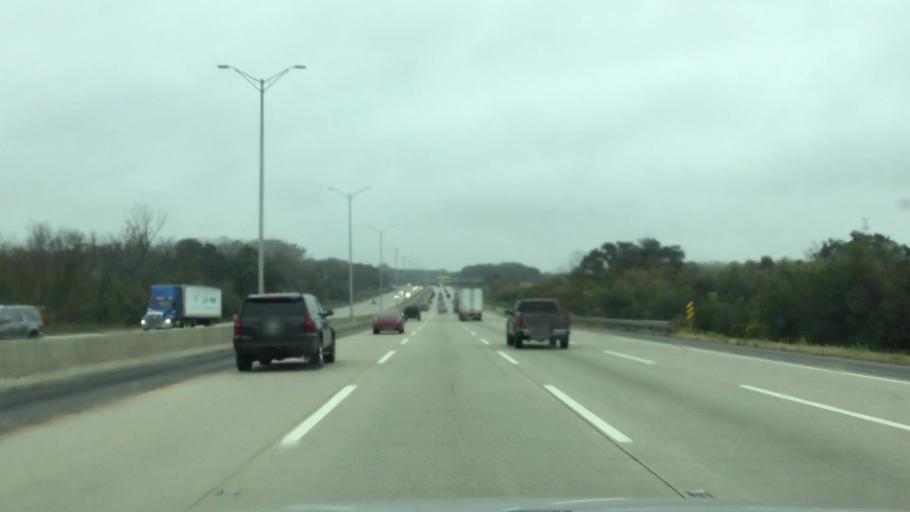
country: US
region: Illinois
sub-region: Lake County
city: Wadsworth
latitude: 42.4161
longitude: -87.9477
